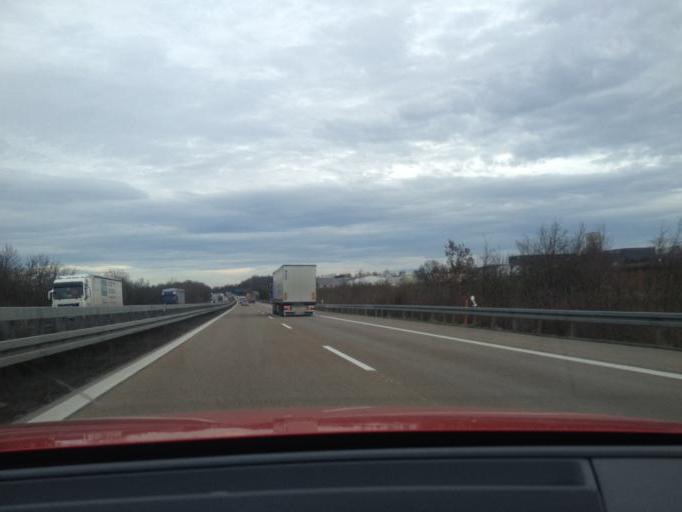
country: DE
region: Baden-Wuerttemberg
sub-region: Regierungsbezirk Stuttgart
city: Wolpertshausen
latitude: 49.1743
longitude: 9.8537
